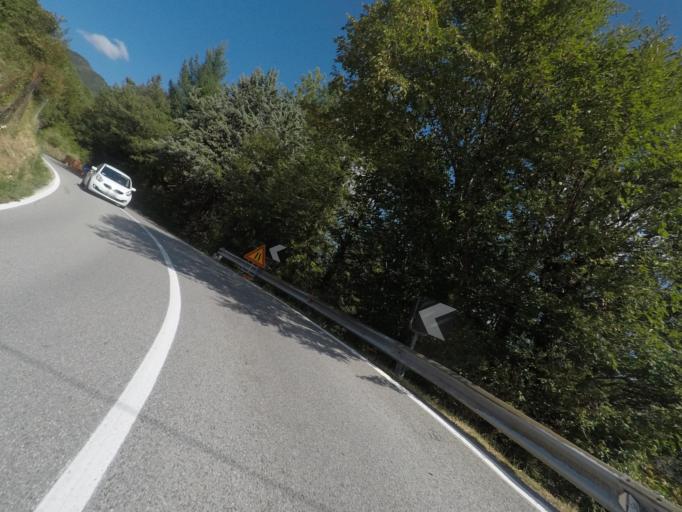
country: IT
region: Tuscany
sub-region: Provincia di Massa-Carrara
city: Fivizzano
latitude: 44.2575
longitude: 10.1728
